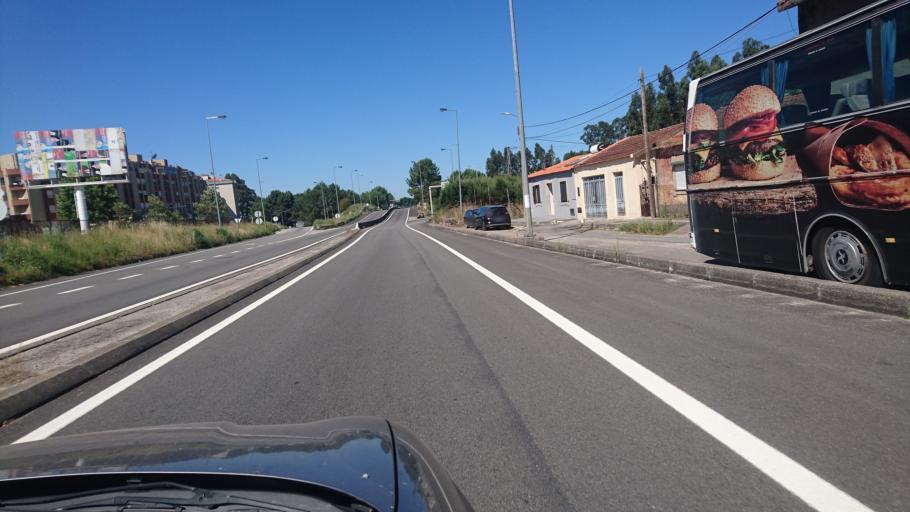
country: PT
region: Aveiro
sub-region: Santa Maria da Feira
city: Feira
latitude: 40.9258
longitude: -8.5620
